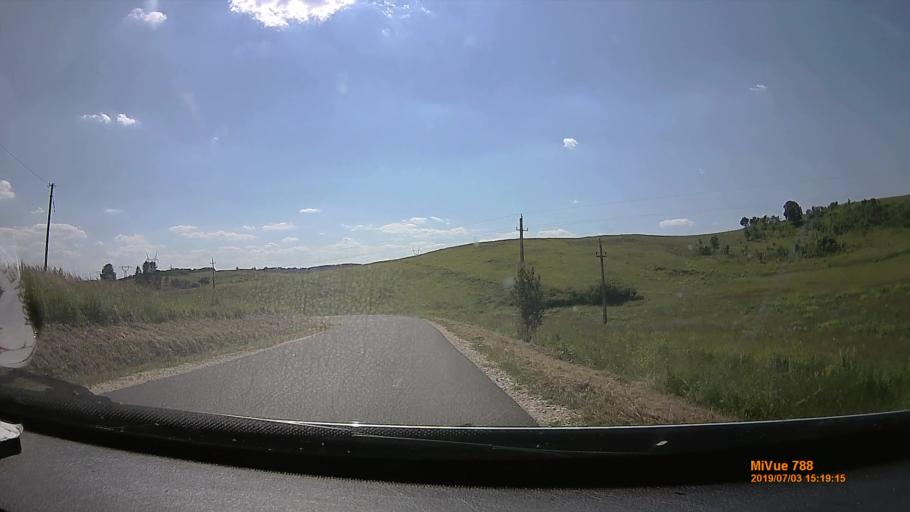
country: HU
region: Borsod-Abauj-Zemplen
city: Farkaslyuk
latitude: 48.2021
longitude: 20.3896
